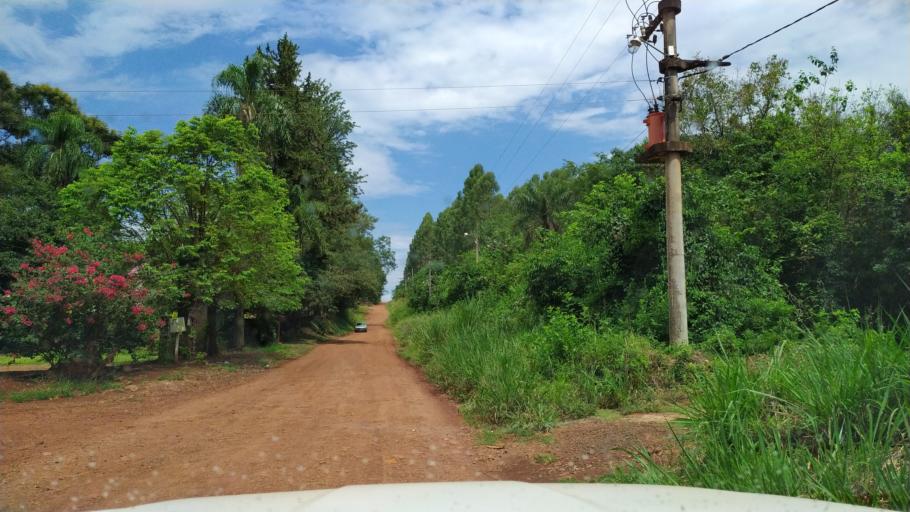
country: AR
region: Misiones
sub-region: Departamento de Eldorado
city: Eldorado
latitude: -26.4461
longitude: -54.6040
